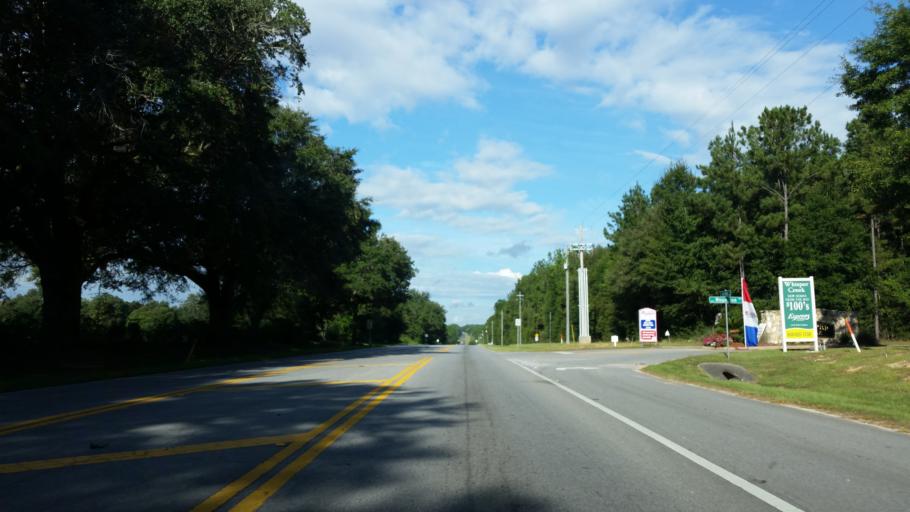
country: US
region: Florida
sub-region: Santa Rosa County
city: Pace
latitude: 30.6468
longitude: -87.1189
